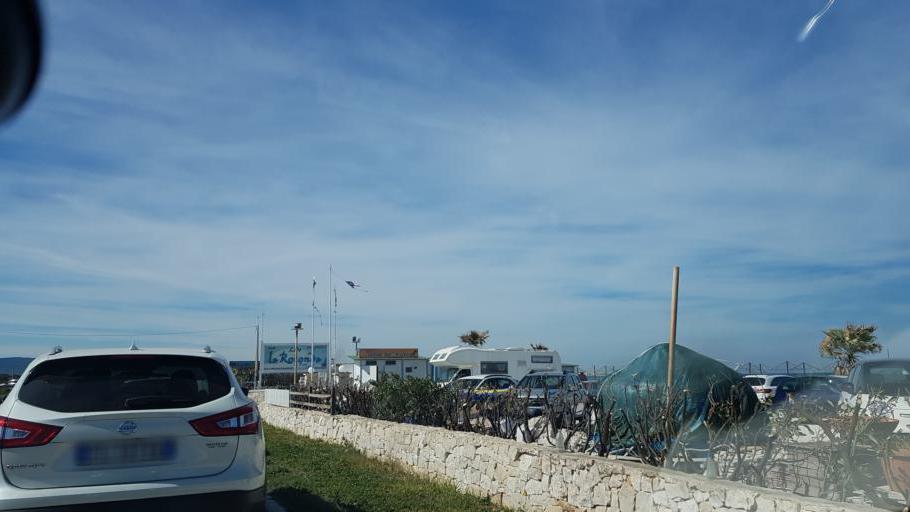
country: IT
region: Apulia
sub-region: Provincia di Brindisi
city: Pezze di Greco
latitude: 40.8566
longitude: 17.4387
